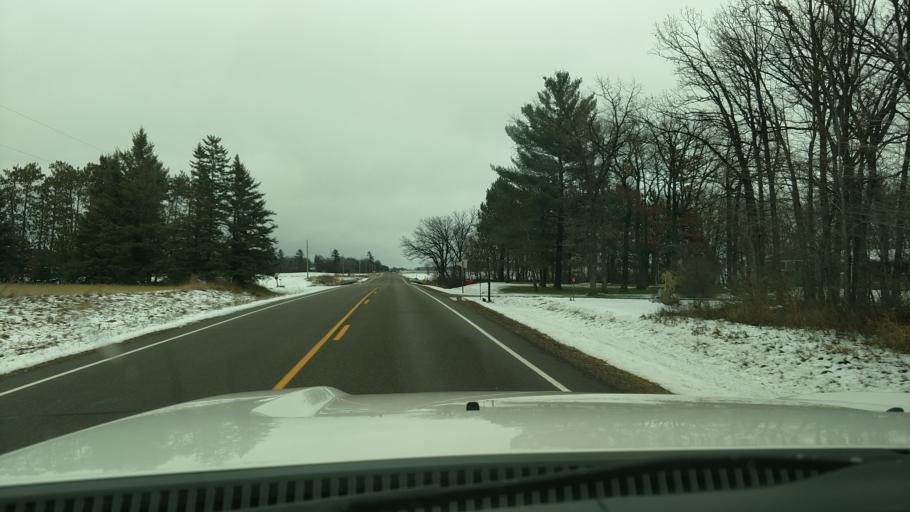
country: US
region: Wisconsin
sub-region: Dunn County
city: Colfax
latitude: 45.1427
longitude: -91.6968
